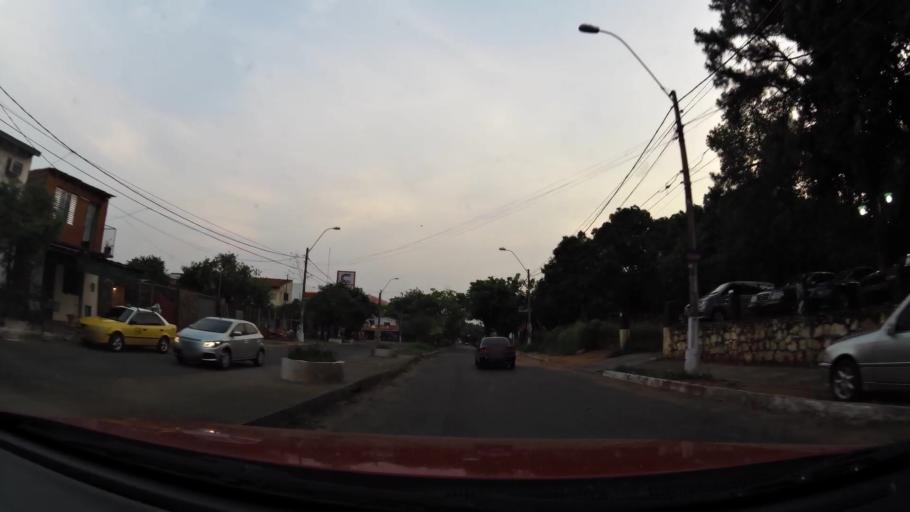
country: PY
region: Asuncion
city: Asuncion
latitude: -25.3187
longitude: -57.6140
